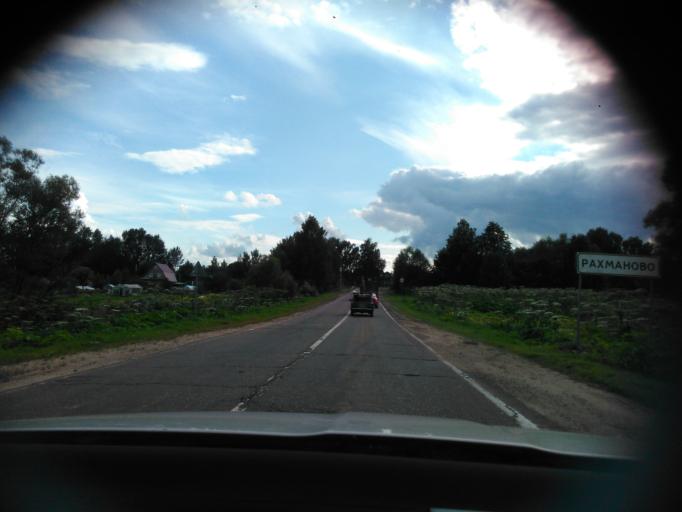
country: RU
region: Moskovskaya
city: Klin
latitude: 56.1555
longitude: 36.7540
